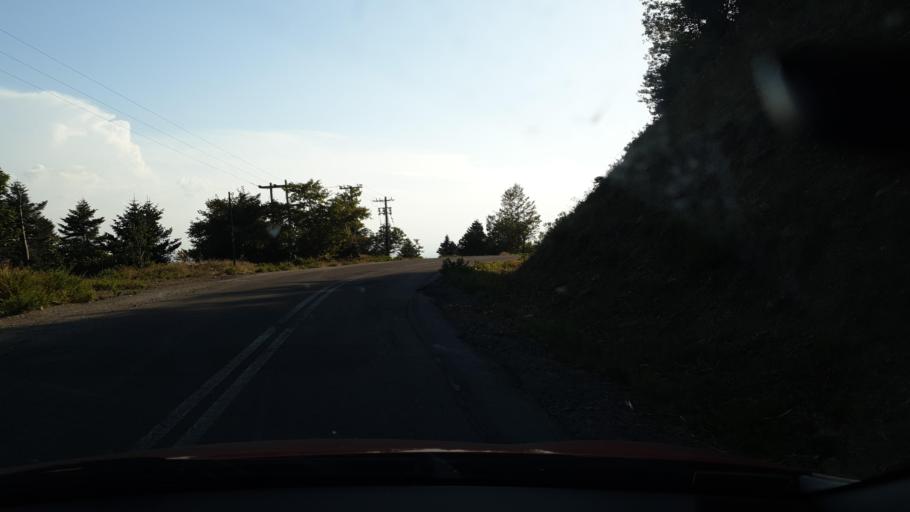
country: GR
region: Central Greece
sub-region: Nomos Evvoias
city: Yimnon
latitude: 38.6033
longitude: 23.8582
